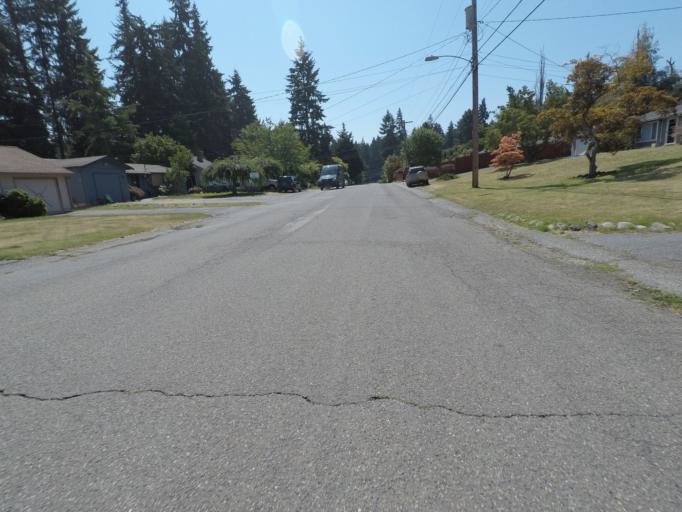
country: US
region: Washington
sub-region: King County
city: Inglewood-Finn Hill
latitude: 47.7294
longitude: -122.2405
